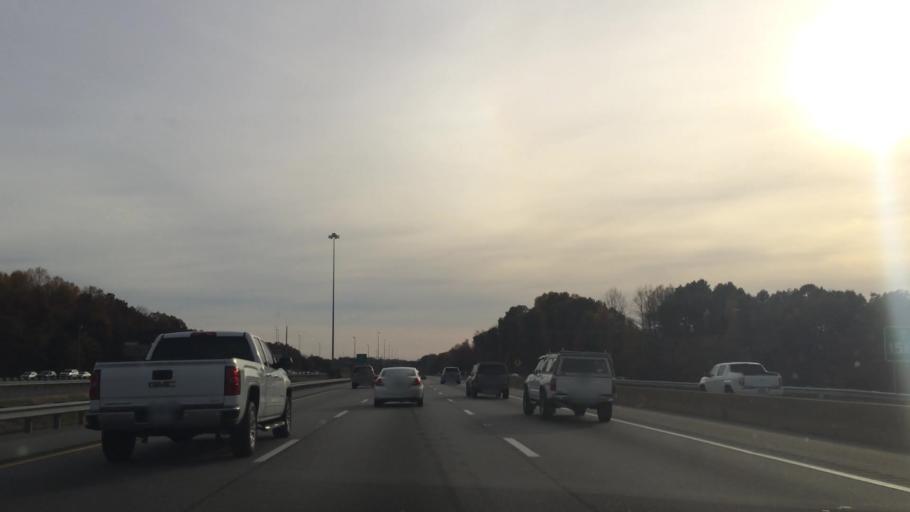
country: US
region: Virginia
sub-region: Prince William County
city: Potomac Mills
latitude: 38.6267
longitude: -77.2942
